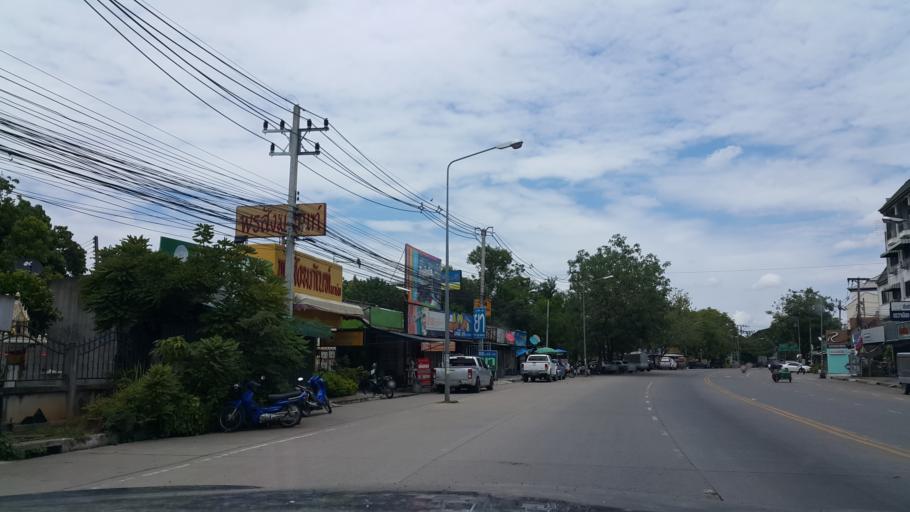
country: TH
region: Chiang Mai
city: Chiang Mai
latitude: 18.8012
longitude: 98.9996
